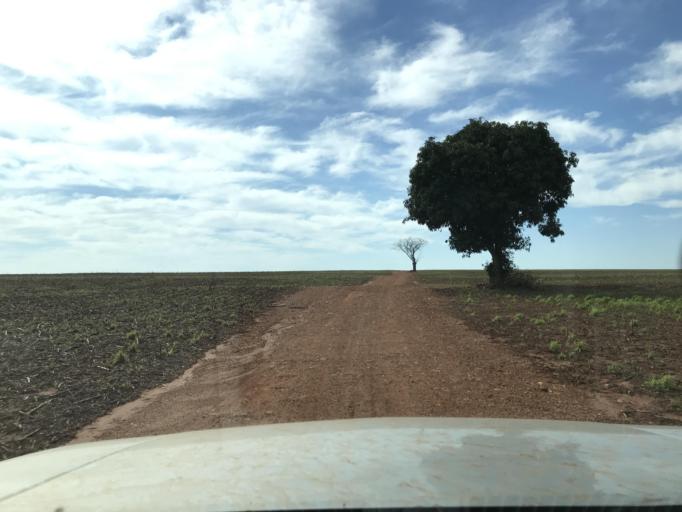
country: BR
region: Parana
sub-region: Palotina
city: Palotina
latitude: -24.1875
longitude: -53.8342
